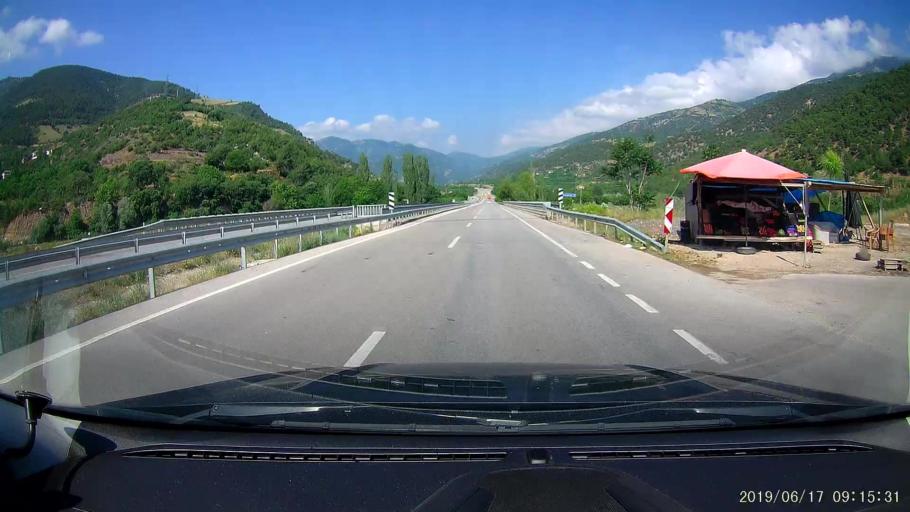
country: TR
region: Amasya
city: Akdag
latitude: 40.7467
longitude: 36.0345
